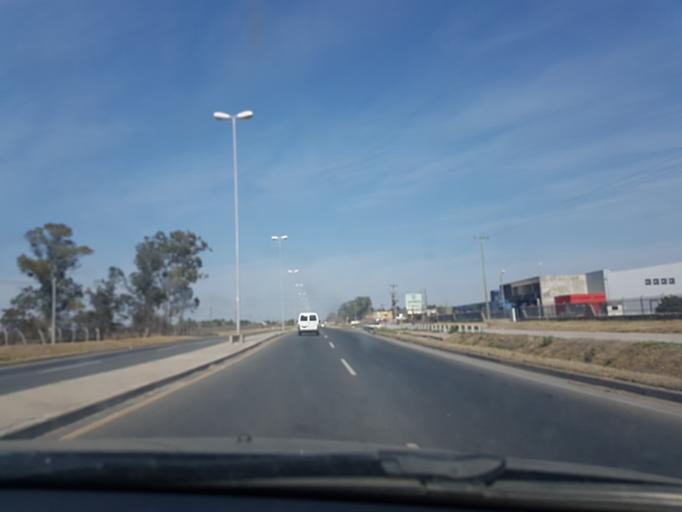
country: AR
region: Cordoba
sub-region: Departamento de Capital
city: Cordoba
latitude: -31.4875
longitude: -64.2478
